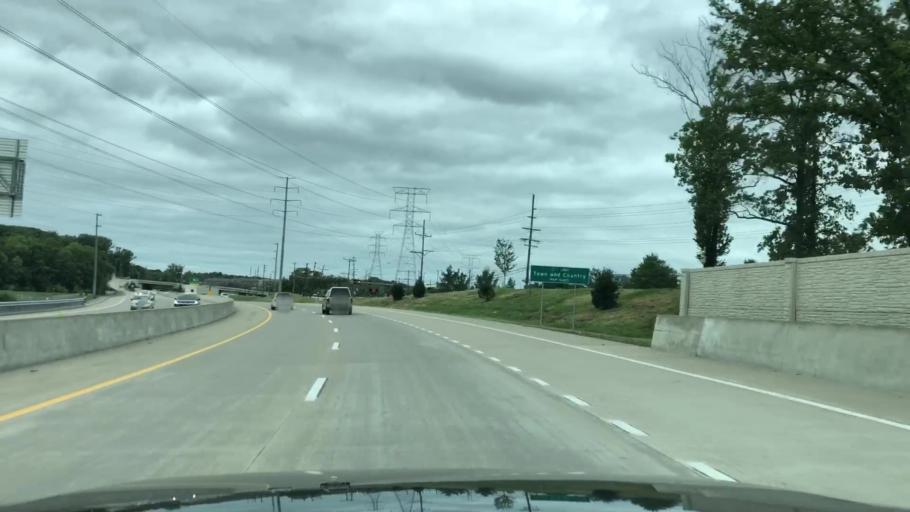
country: US
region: Missouri
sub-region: Saint Louis County
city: Town and Country
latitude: 38.6665
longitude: -90.5016
